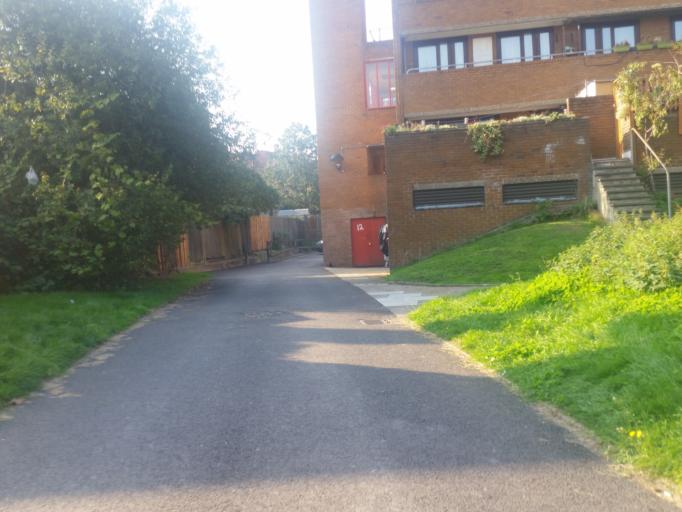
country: GB
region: England
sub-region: Greater London
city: Harringay
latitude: 51.5934
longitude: -0.1041
